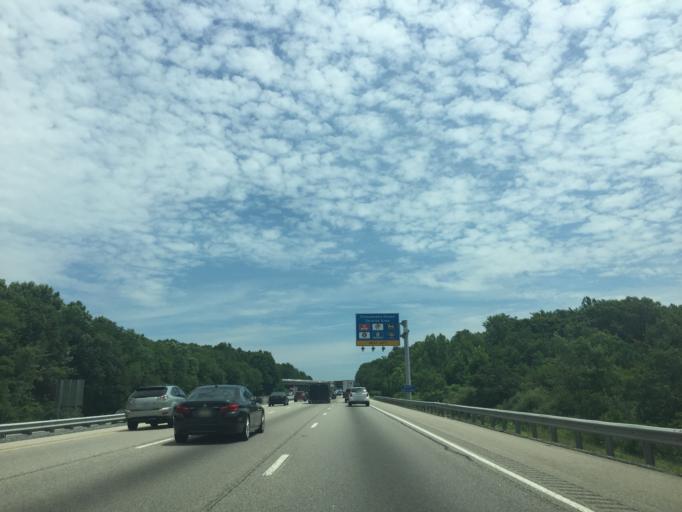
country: US
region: Maryland
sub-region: Cecil County
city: Perryville
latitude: 39.6061
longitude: -76.0292
